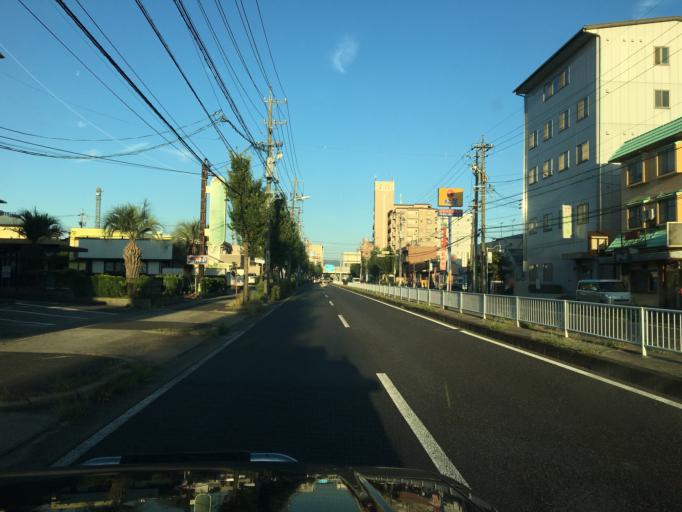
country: JP
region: Aichi
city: Kasugai
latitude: 35.1924
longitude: 137.0076
